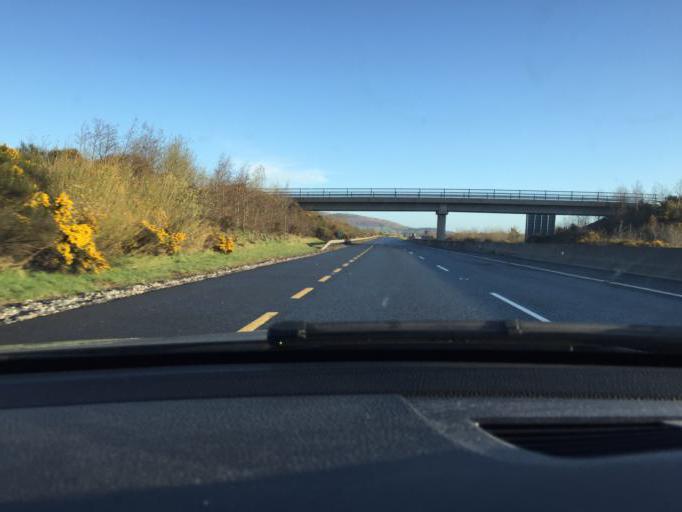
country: GB
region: Northern Ireland
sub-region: Newry and Mourne District
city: Newry
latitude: 54.1071
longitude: -6.3651
